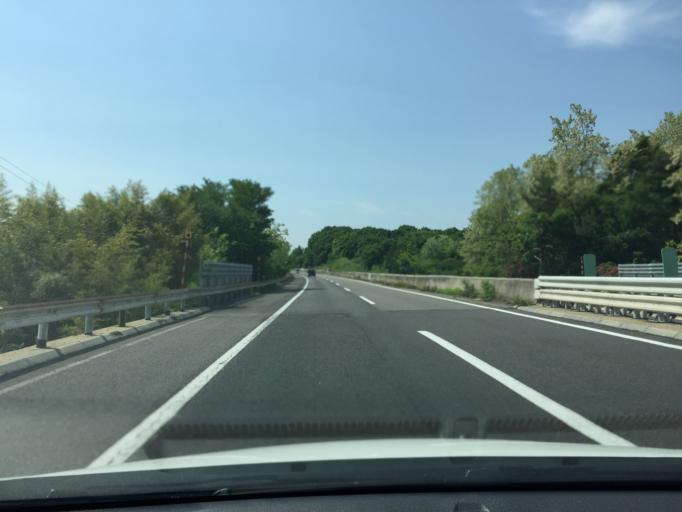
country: JP
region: Fukushima
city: Sukagawa
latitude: 37.3142
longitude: 140.3437
